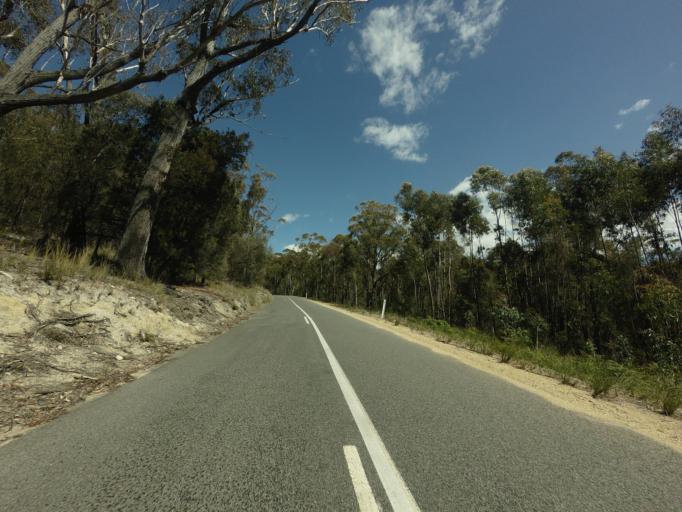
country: AU
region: Tasmania
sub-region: Break O'Day
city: St Helens
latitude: -41.6624
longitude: 148.2699
